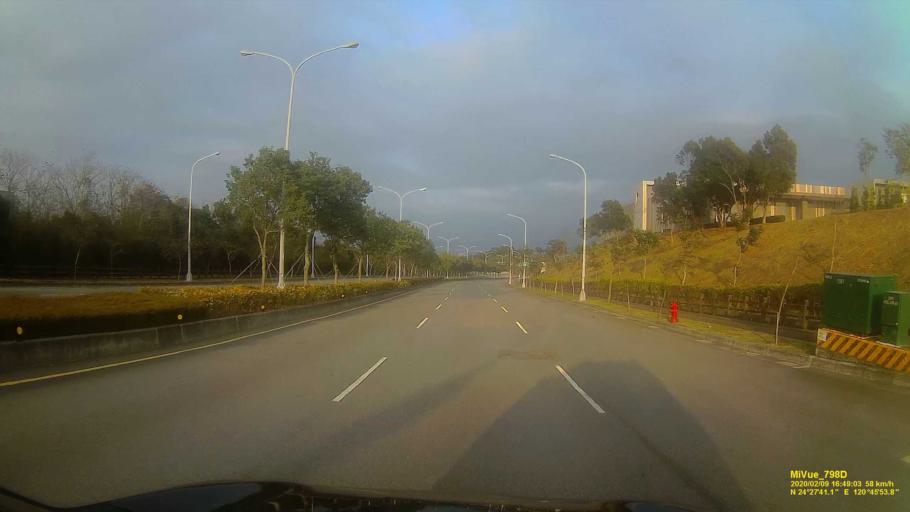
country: TW
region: Taiwan
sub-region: Miaoli
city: Miaoli
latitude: 24.4615
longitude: 120.7650
